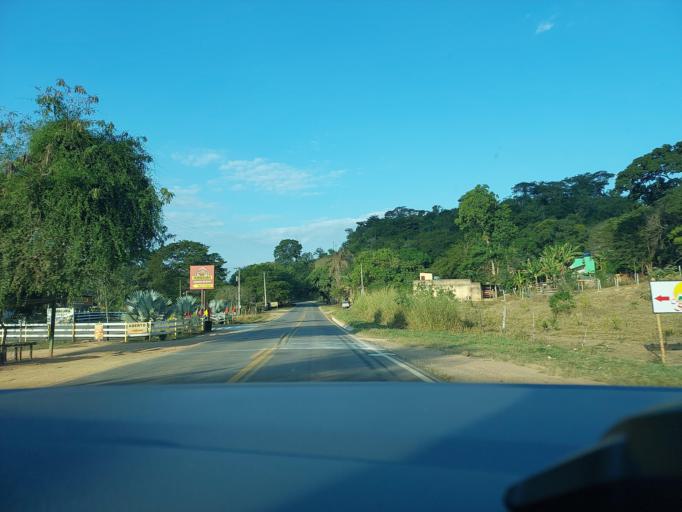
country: BR
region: Minas Gerais
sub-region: Muriae
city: Muriae
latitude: -21.1202
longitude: -42.4132
